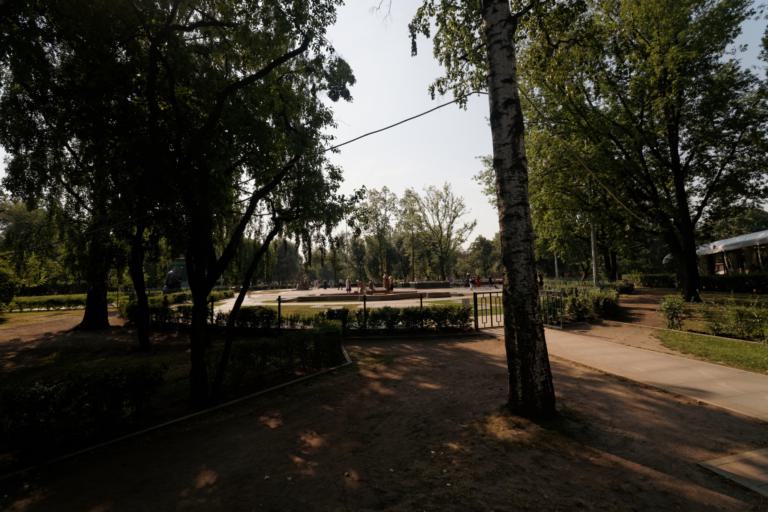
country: RU
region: St.-Petersburg
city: Petrogradka
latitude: 59.9561
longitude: 30.3163
